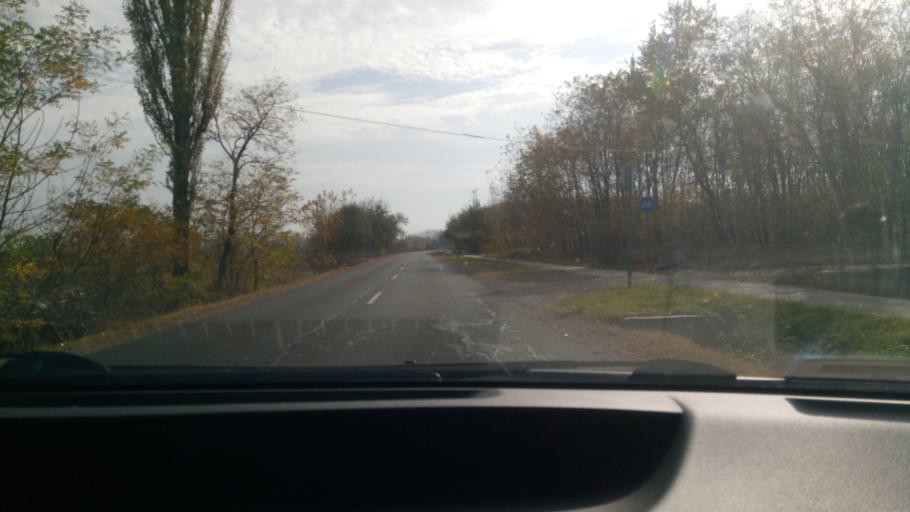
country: HU
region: Bacs-Kiskun
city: Kiskunmajsa
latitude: 46.5288
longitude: 19.7422
